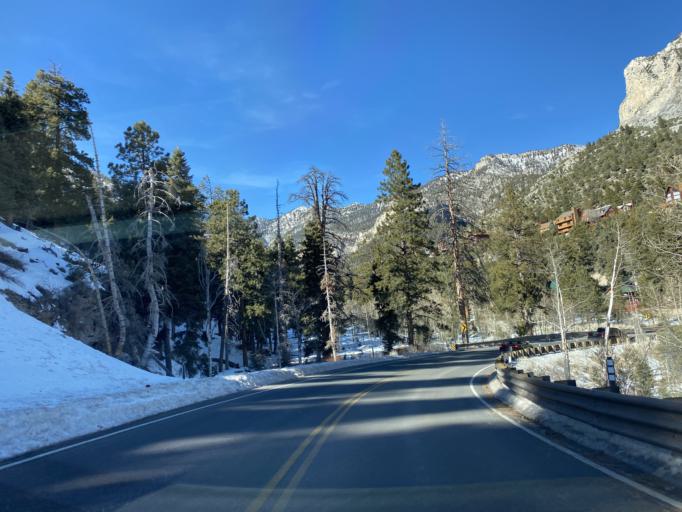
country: US
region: Nevada
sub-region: Nye County
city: Pahrump
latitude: 36.2610
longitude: -115.6528
